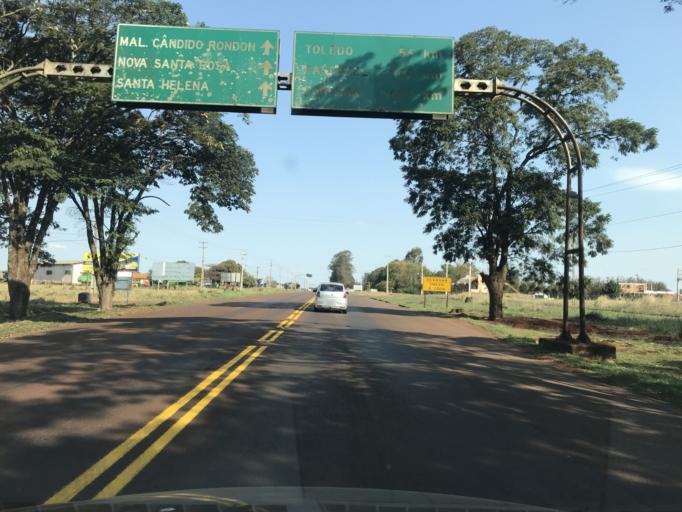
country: BR
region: Parana
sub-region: Palotina
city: Palotina
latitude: -24.3063
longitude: -53.8332
